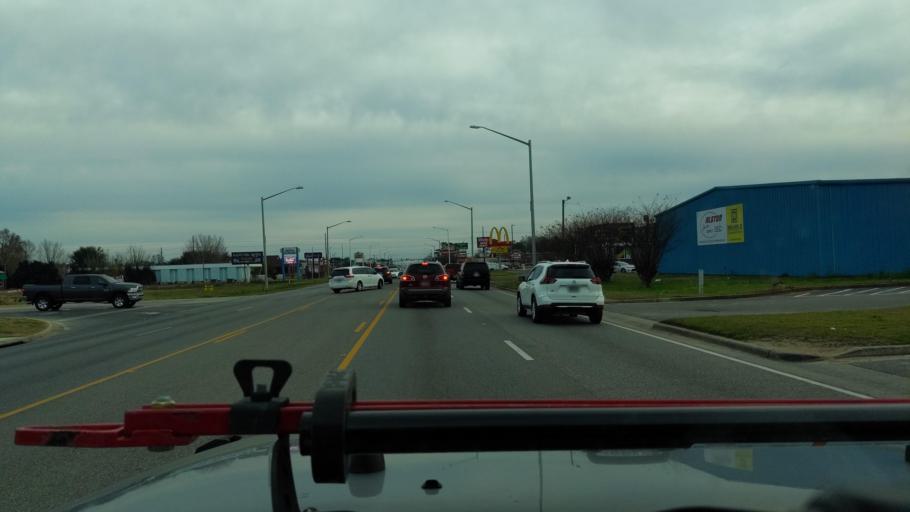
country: US
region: Alabama
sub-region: Baldwin County
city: Foley
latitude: 30.3961
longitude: -87.6834
